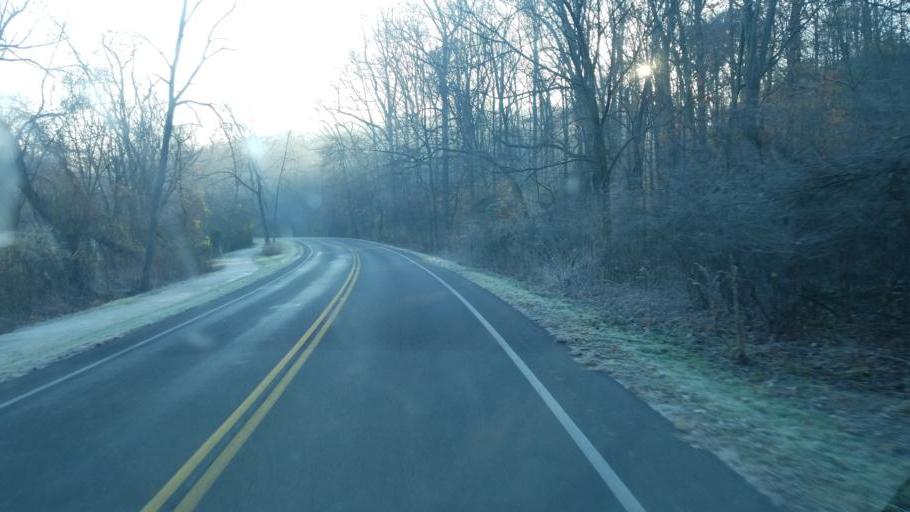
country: US
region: Ohio
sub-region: Summit County
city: Fairlawn
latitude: 41.1298
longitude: -81.5554
